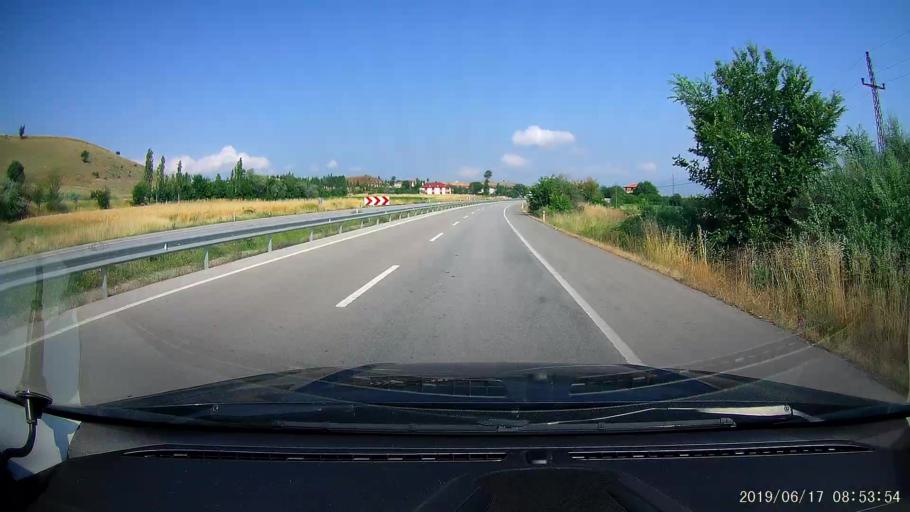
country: TR
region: Amasya
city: Esencay
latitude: 40.7138
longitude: 36.4719
